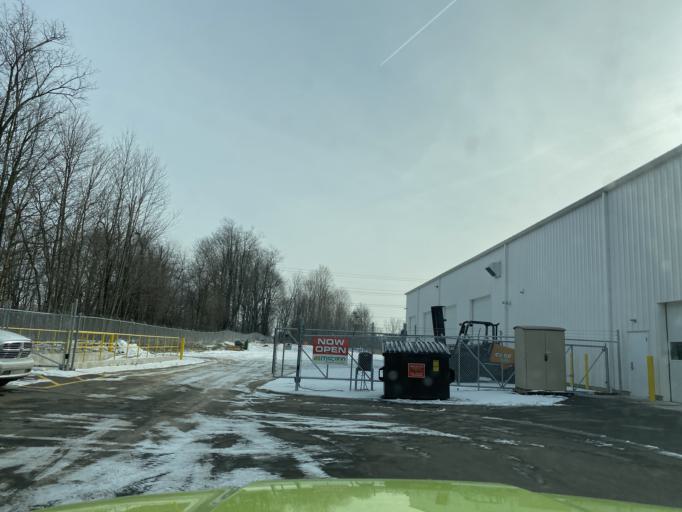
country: US
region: Michigan
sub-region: Kent County
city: Walker
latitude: 43.0360
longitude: -85.8140
